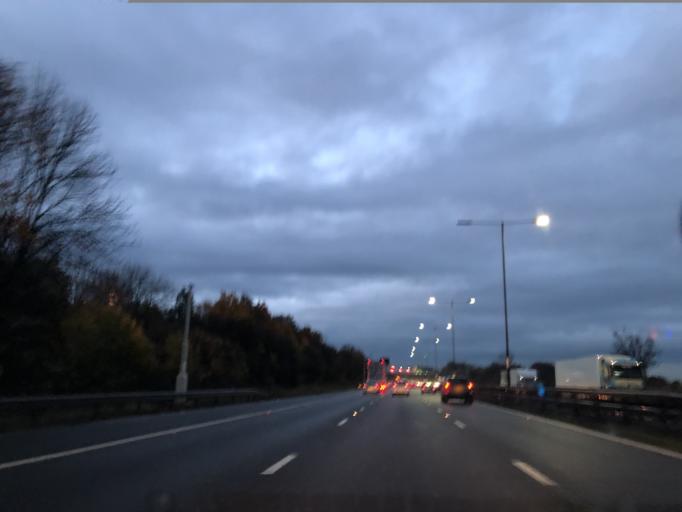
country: GB
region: England
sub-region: Solihull
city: Chelmsley Wood
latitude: 52.4943
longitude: -1.7352
